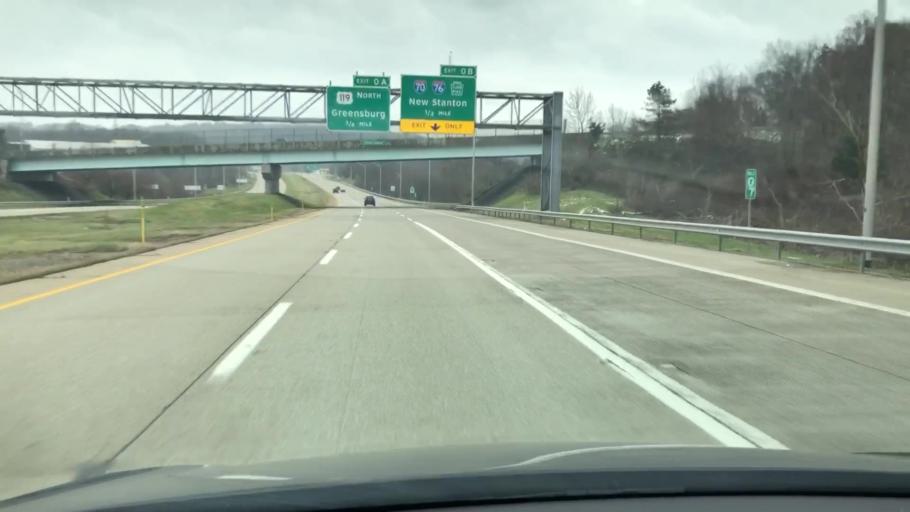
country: US
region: Pennsylvania
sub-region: Westmoreland County
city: New Stanton
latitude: 40.2336
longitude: -79.6020
